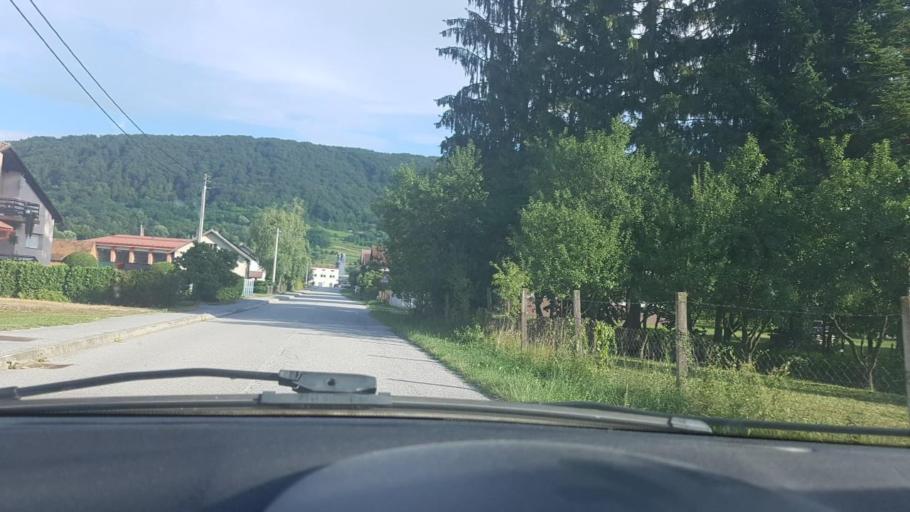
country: HR
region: Varazdinska
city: Lepoglava
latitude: 46.2291
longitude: 15.9784
